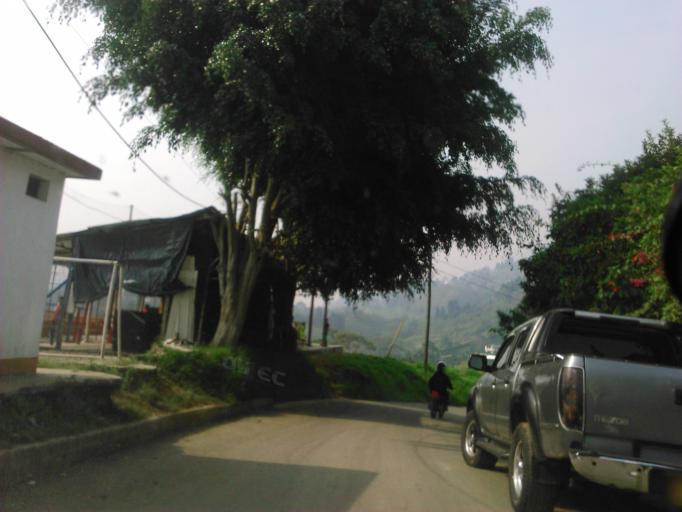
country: CO
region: Antioquia
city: La Estrella
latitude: 6.1377
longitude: -75.6411
